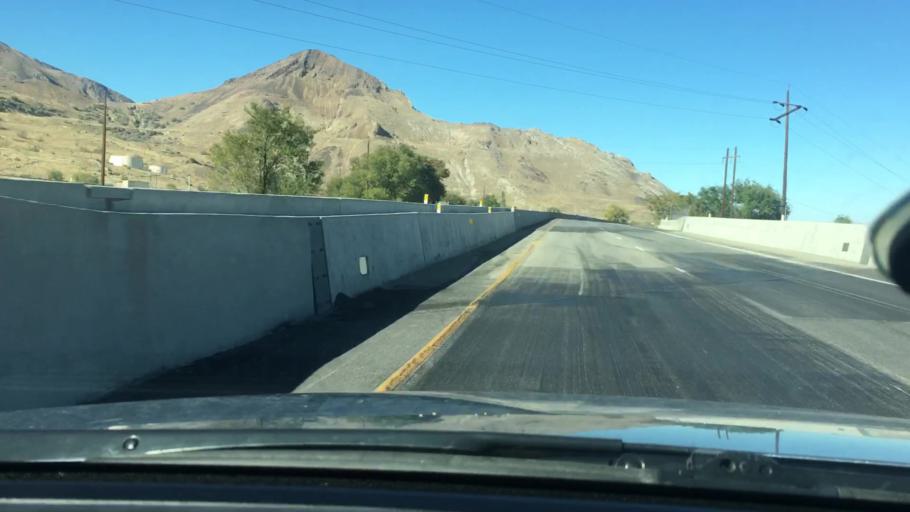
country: US
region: Utah
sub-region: Salt Lake County
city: Magna
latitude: 40.7214
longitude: -112.1544
